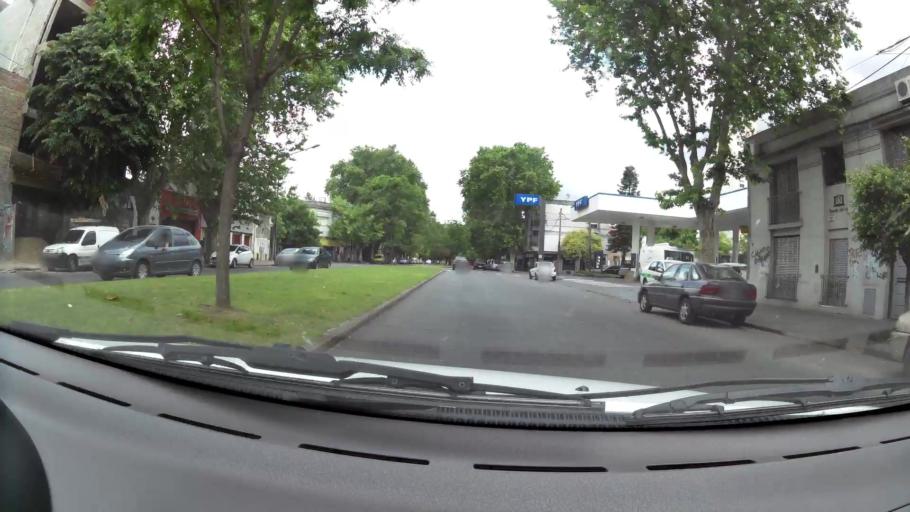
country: AR
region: Buenos Aires
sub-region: Partido de La Plata
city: La Plata
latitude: -34.9176
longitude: -57.9324
